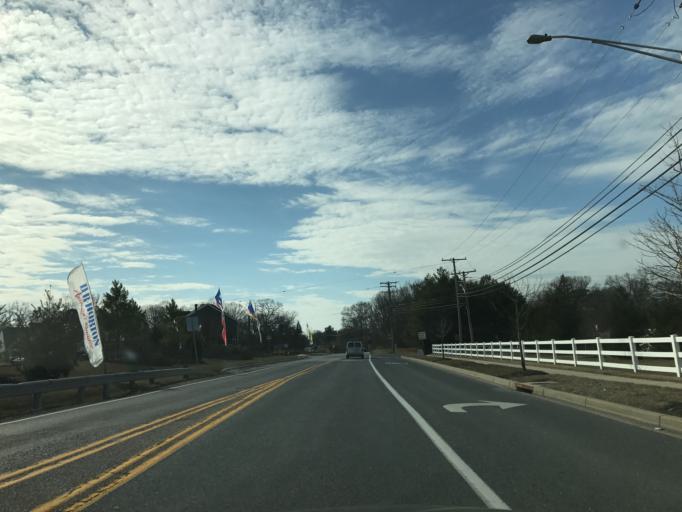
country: US
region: Maryland
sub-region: Anne Arundel County
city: South Gate
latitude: 39.1210
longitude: -76.6454
